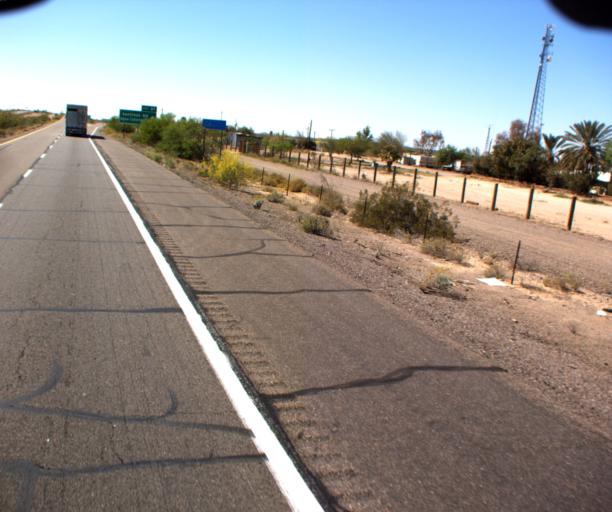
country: US
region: Arizona
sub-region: Maricopa County
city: Gila Bend
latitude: 32.8593
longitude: -113.2059
